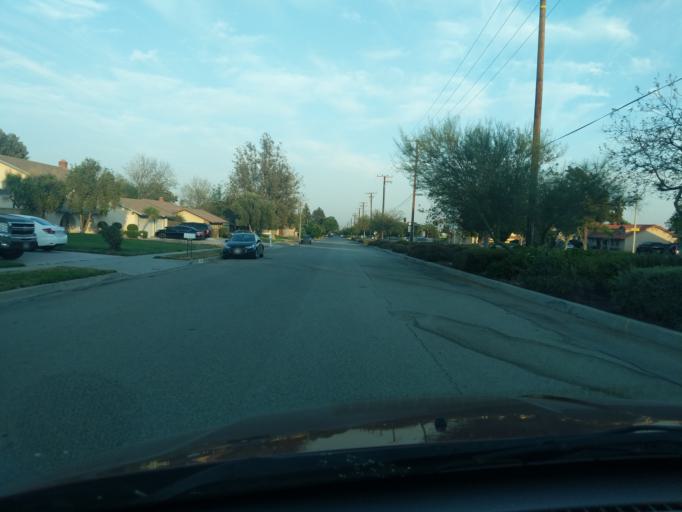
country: US
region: California
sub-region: San Bernardino County
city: Muscoy
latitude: 34.1522
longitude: -117.3925
